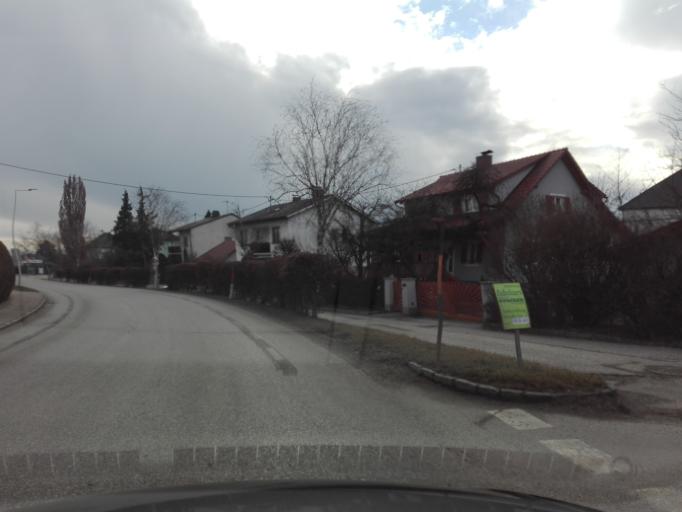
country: AT
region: Upper Austria
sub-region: Politischer Bezirk Perg
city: Perg
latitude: 48.2732
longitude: 14.5776
